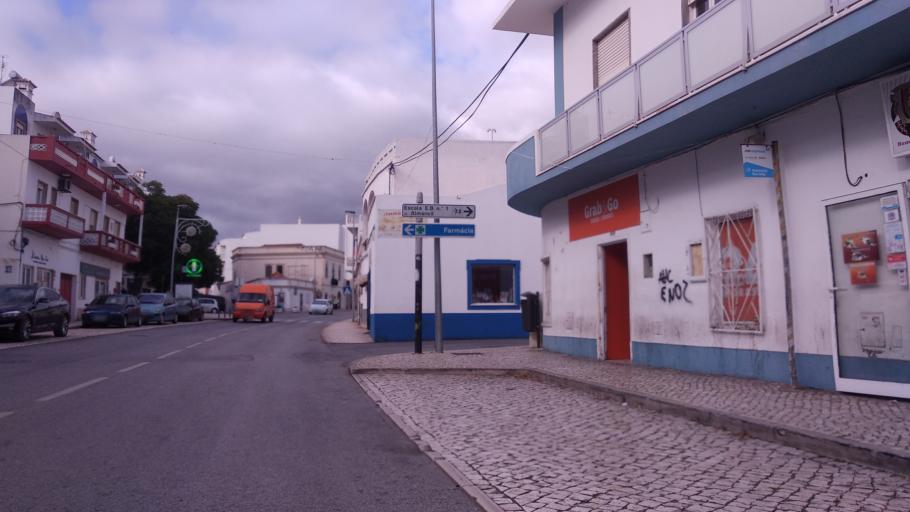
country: PT
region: Faro
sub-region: Loule
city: Almancil
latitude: 37.0872
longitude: -8.0320
